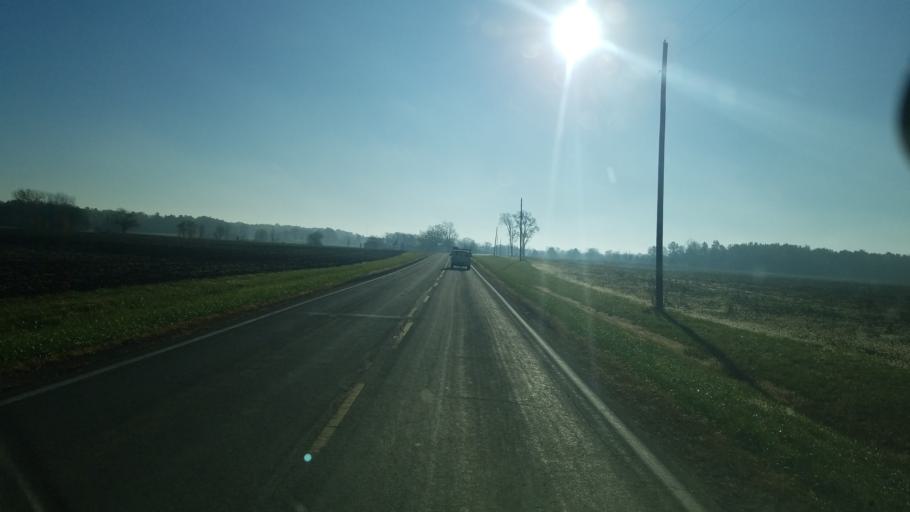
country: US
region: Ohio
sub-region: Morrow County
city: Cardington
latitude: 40.5153
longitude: -82.9244
